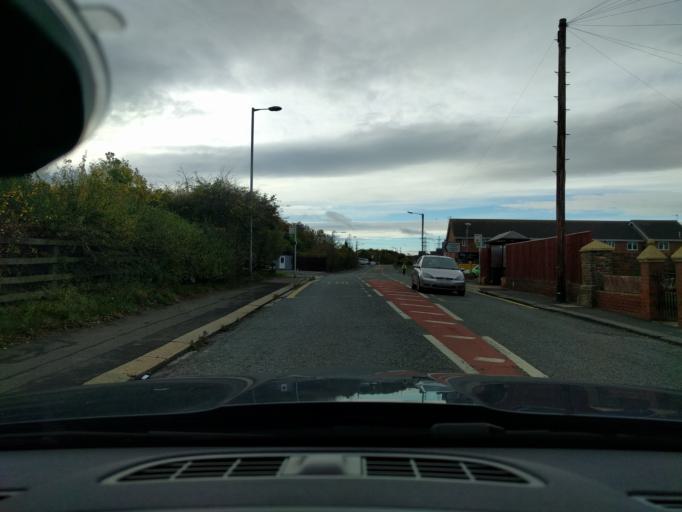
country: GB
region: England
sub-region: Northumberland
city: Bedlington
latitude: 55.1262
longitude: -1.5629
